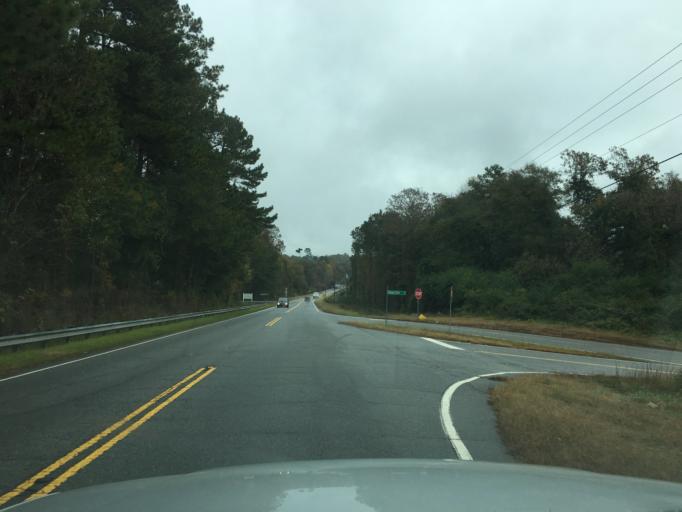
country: US
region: South Carolina
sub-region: Pickens County
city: Clemson
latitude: 34.7892
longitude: -82.8876
